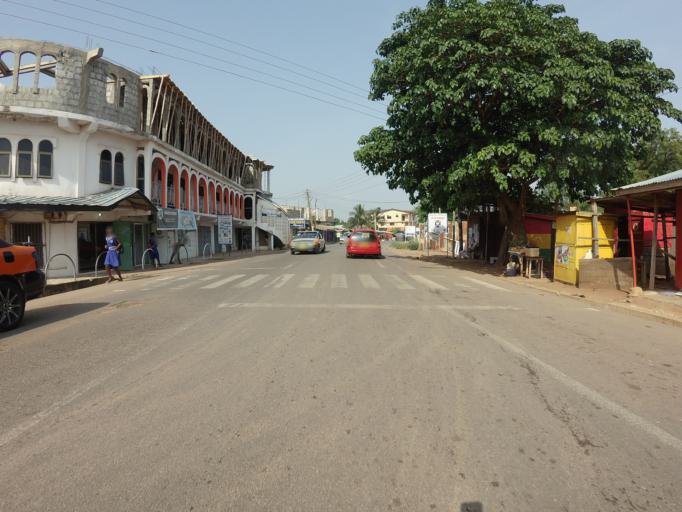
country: GH
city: Akropong
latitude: 6.1077
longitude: -0.0115
